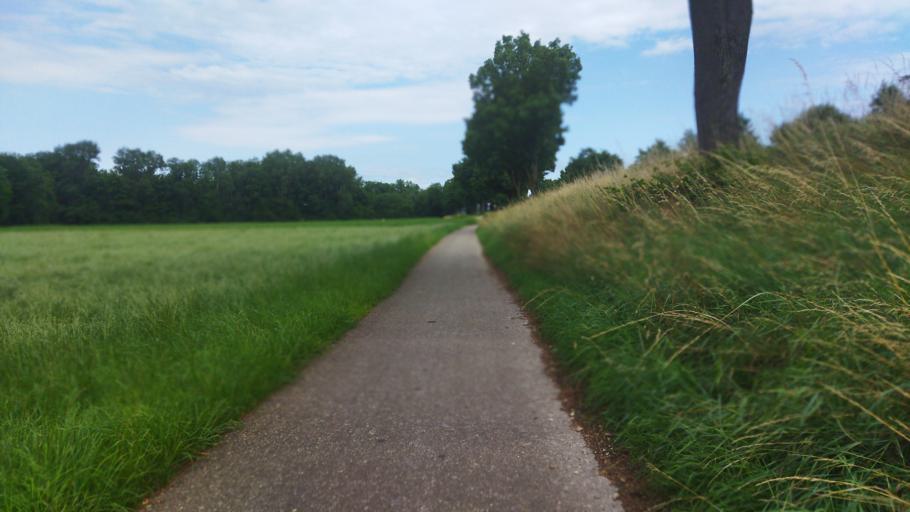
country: DE
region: Bavaria
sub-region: Upper Palatinate
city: Mintraching
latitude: 48.9805
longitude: 12.2771
